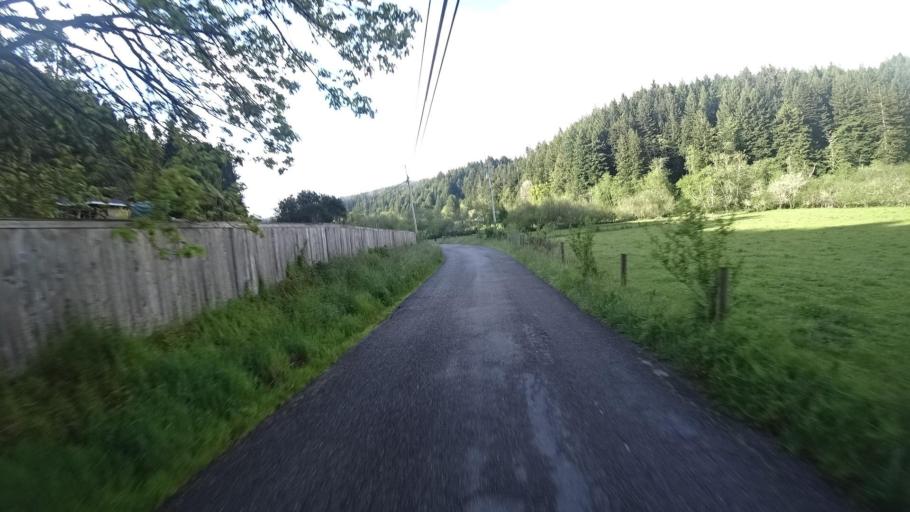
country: US
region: California
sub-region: Humboldt County
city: Arcata
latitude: 40.8922
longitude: -124.0410
